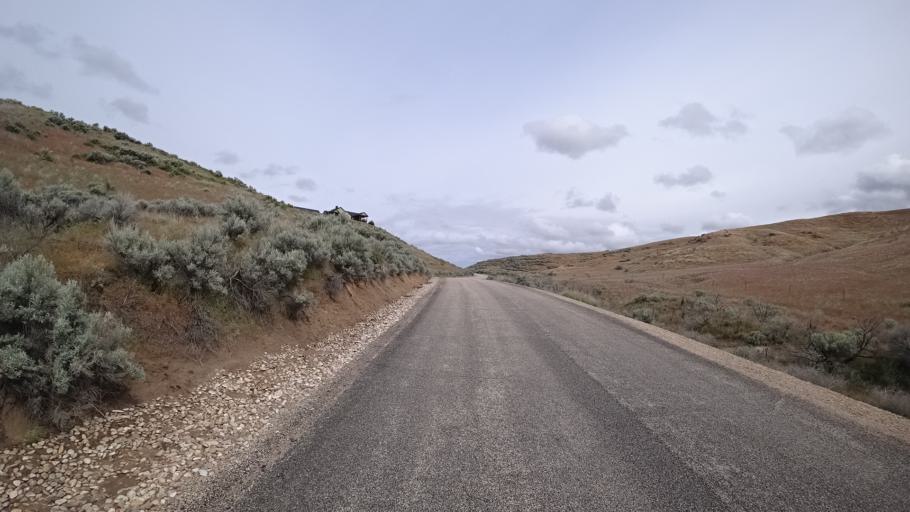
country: US
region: Idaho
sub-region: Ada County
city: Eagle
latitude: 43.7568
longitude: -116.3667
